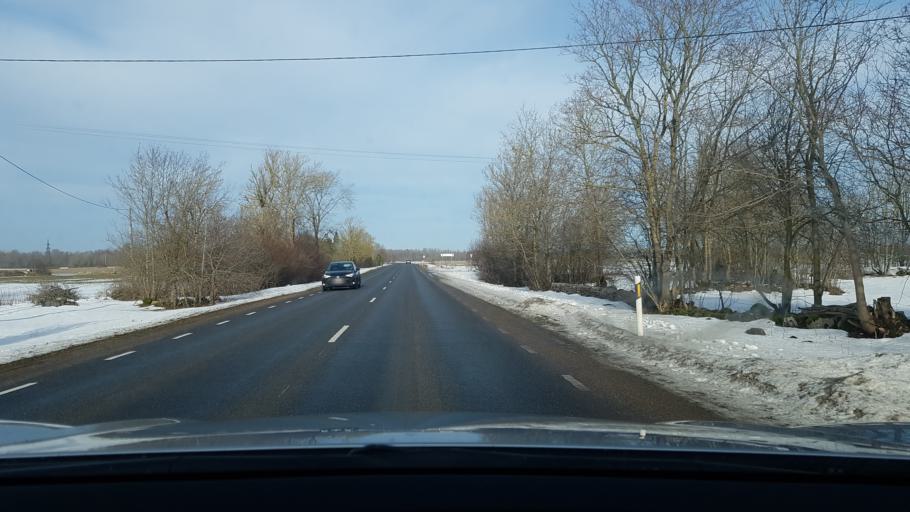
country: EE
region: Saare
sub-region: Kuressaare linn
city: Kuressaare
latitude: 58.2919
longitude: 22.5408
